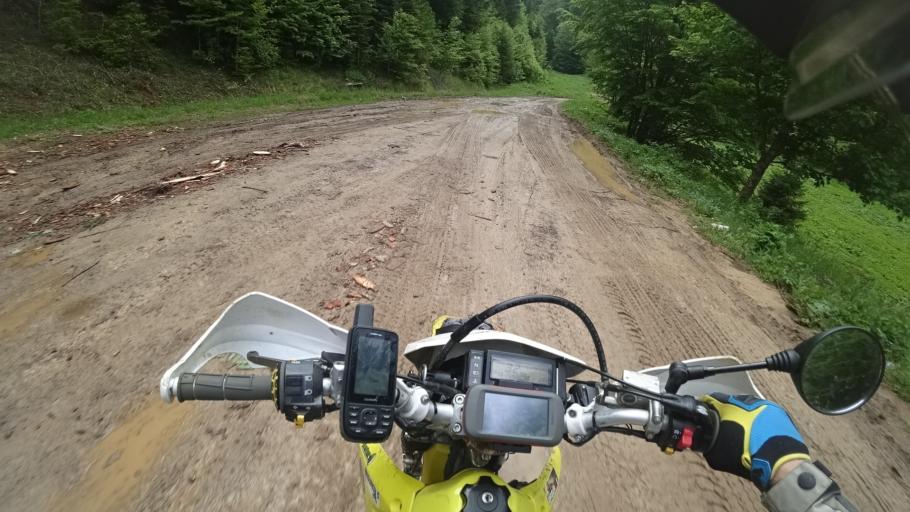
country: BA
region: Federation of Bosnia and Herzegovina
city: Bihac
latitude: 44.6771
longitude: 15.8517
